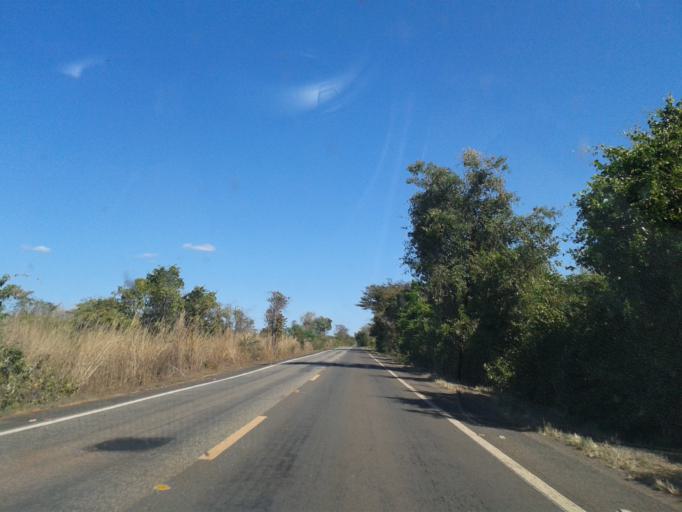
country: BR
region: Goias
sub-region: Crixas
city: Crixas
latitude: -13.9905
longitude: -50.3236
